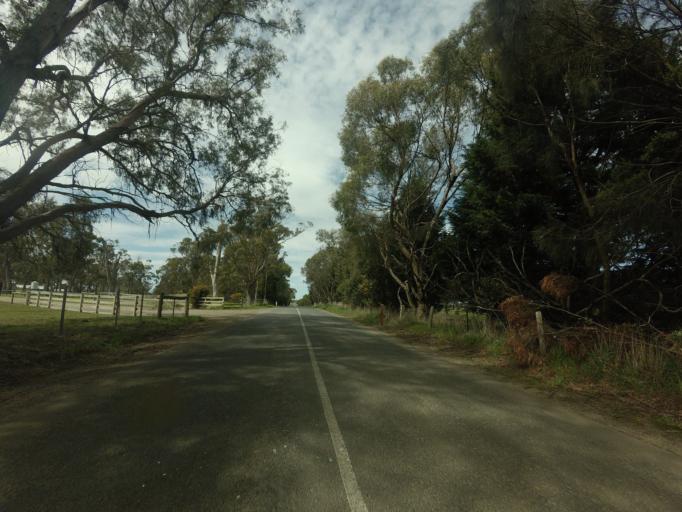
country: AU
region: Tasmania
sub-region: Northern Midlands
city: Longford
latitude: -41.6615
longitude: 147.1758
